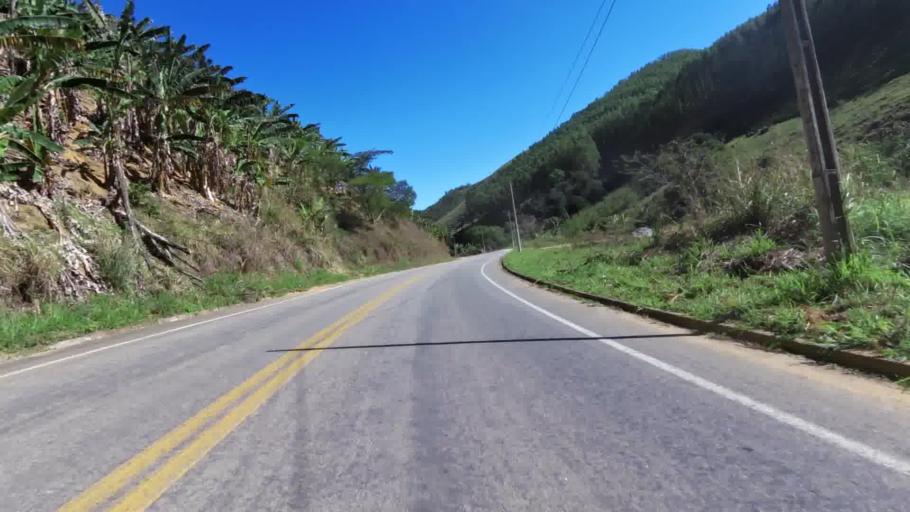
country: BR
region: Espirito Santo
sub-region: Iconha
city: Iconha
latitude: -20.7472
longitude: -40.8608
